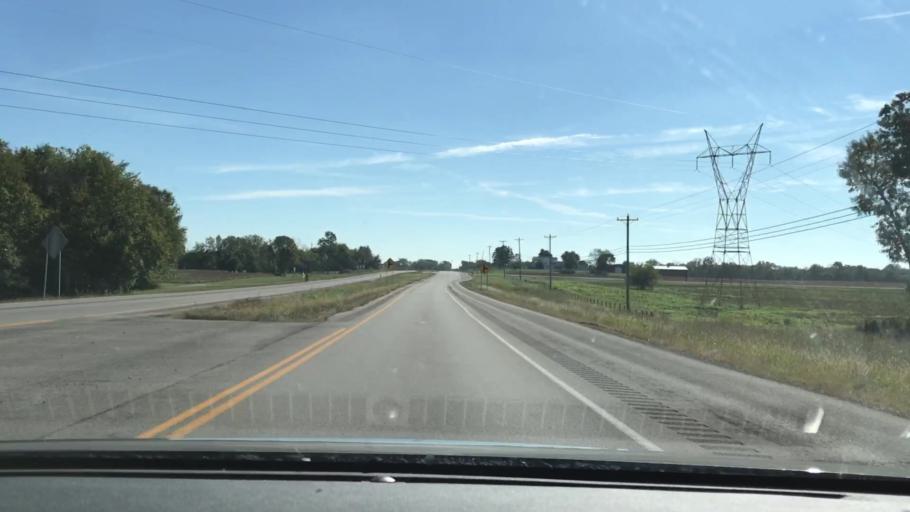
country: US
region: Kentucky
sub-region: Christian County
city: Hopkinsville
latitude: 36.8586
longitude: -87.4284
